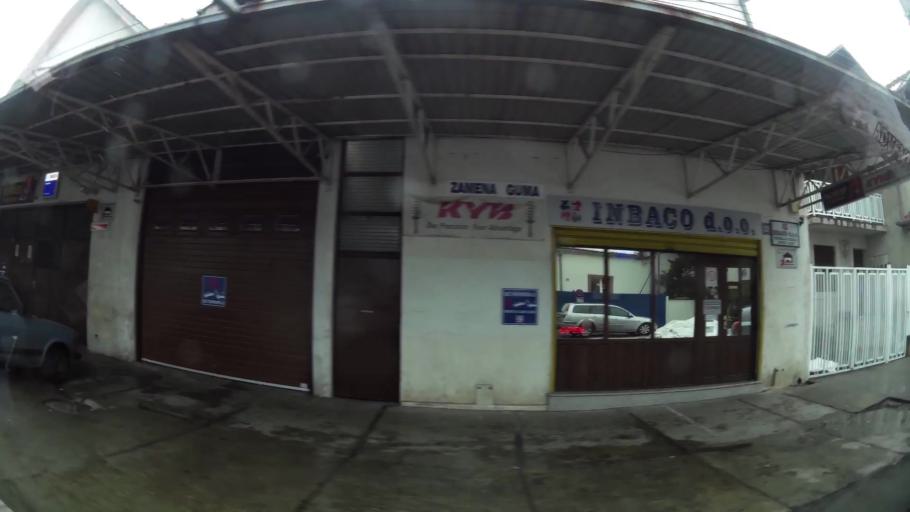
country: RS
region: Central Serbia
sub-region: Belgrade
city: Zemun
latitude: 44.8523
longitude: 20.3843
